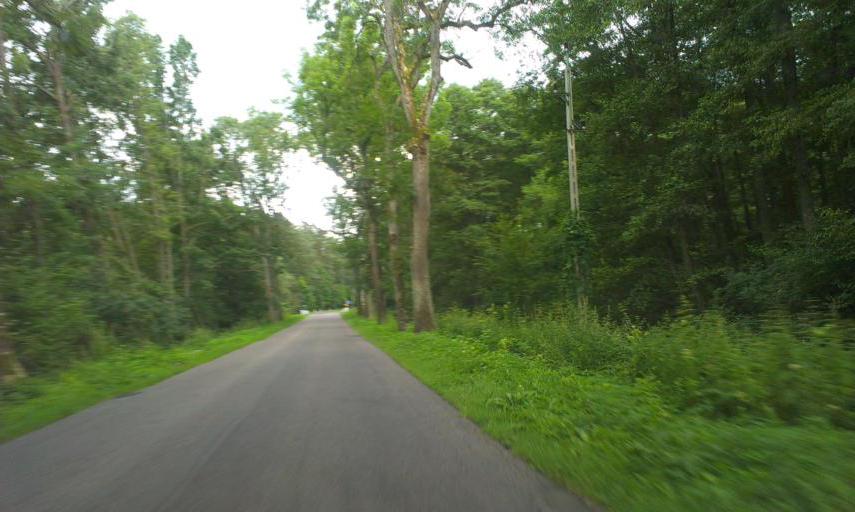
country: PL
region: West Pomeranian Voivodeship
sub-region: Powiat bialogardzki
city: Tychowo
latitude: 53.8744
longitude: 16.1774
